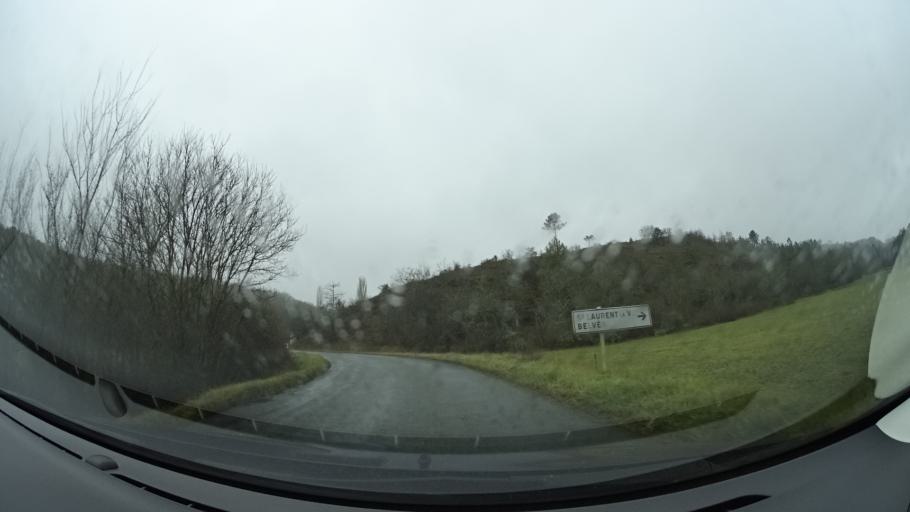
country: FR
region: Aquitaine
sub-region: Departement de la Dordogne
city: Cenac-et-Saint-Julien
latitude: 44.7313
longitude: 1.1368
